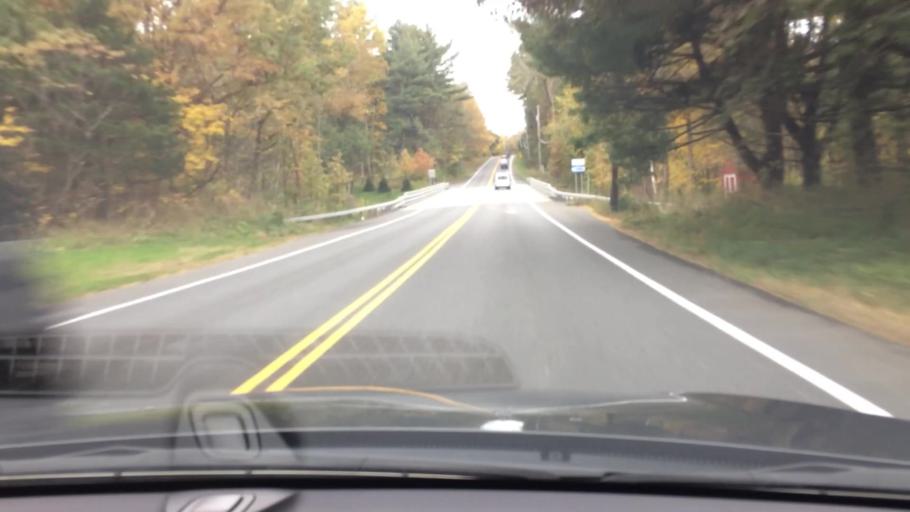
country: US
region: New York
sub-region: Columbia County
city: Oakdale
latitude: 42.1923
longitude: -73.7528
